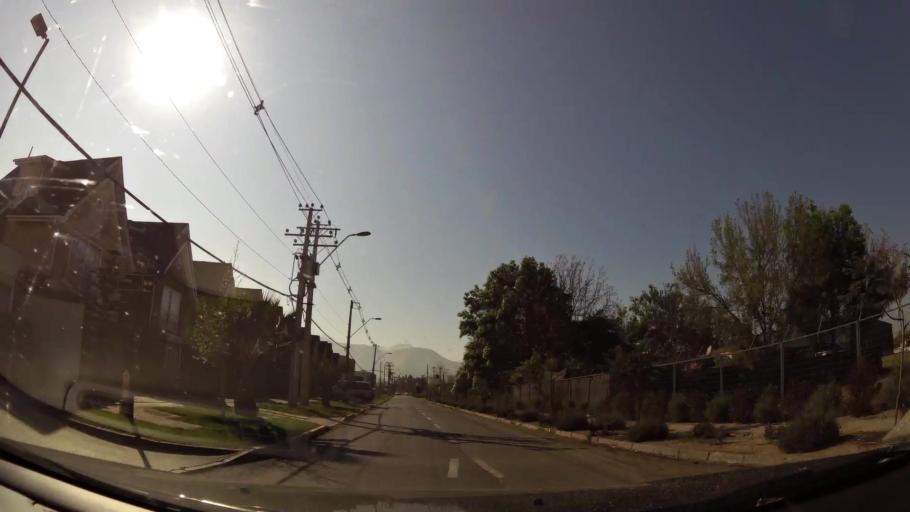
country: CL
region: Santiago Metropolitan
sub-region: Provincia de Chacabuco
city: Chicureo Abajo
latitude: -33.3543
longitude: -70.6817
